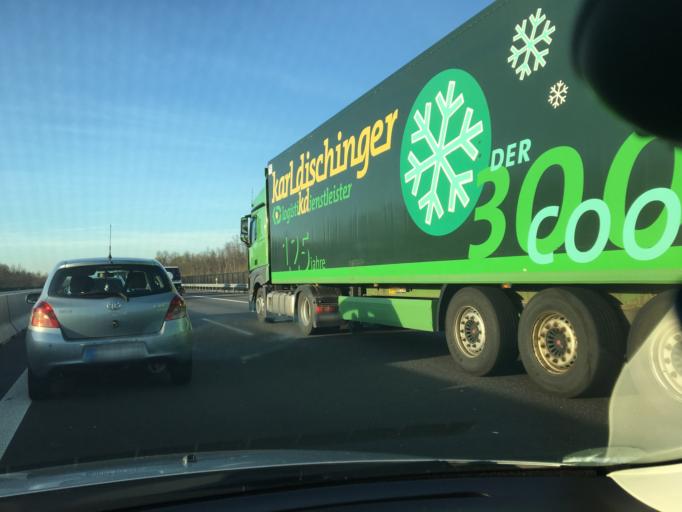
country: DE
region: Baden-Wuerttemberg
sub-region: Freiburg Region
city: Kippenheim
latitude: 48.3273
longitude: 7.7898
